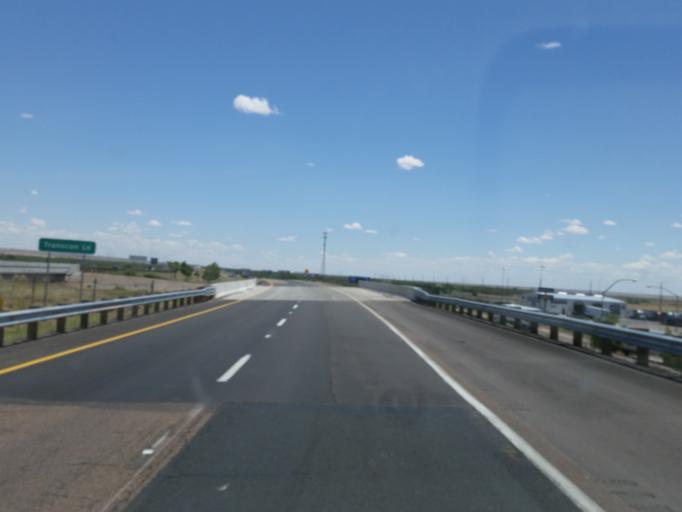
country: US
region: Arizona
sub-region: Navajo County
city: Winslow
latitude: 35.0179
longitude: -110.6749
